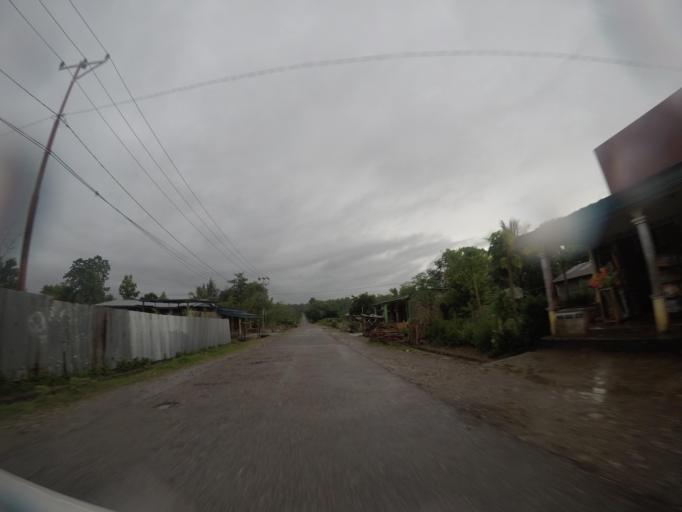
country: TL
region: Bobonaro
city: Maliana
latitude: -8.9619
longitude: 125.1185
